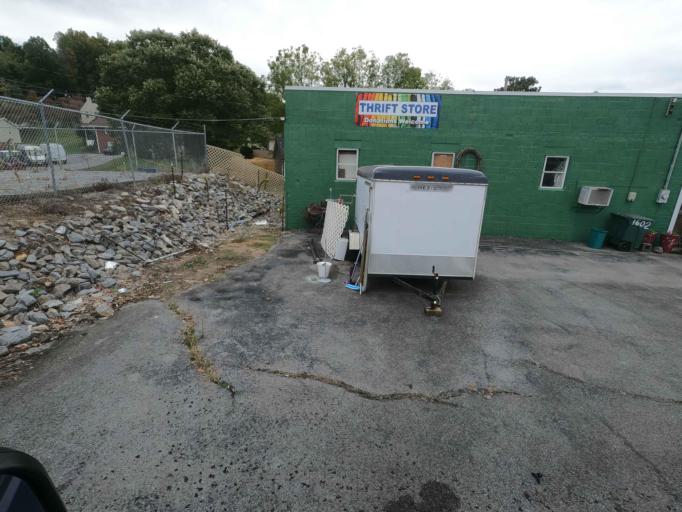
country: US
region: Tennessee
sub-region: Carter County
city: Elizabethton
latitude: 36.3402
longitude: -82.2486
